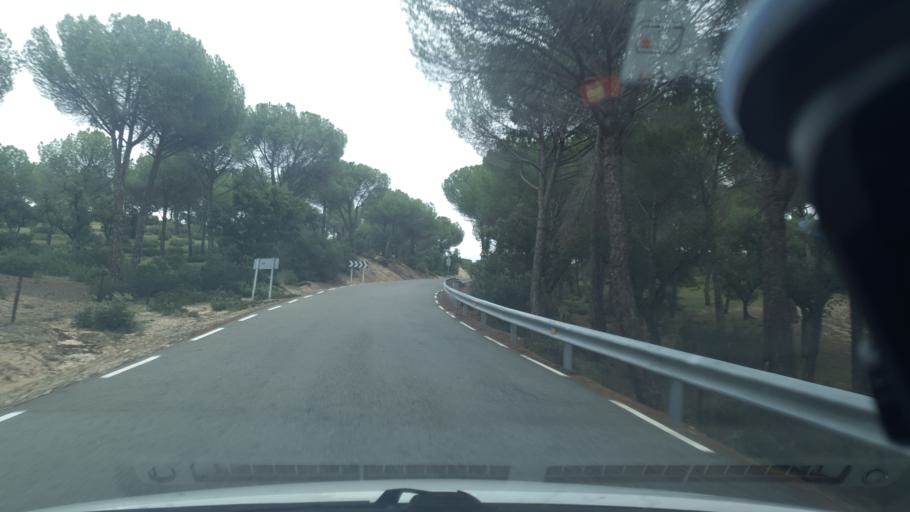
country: ES
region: Castille and Leon
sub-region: Provincia de Avila
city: Pozanco
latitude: 40.8260
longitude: -4.6861
